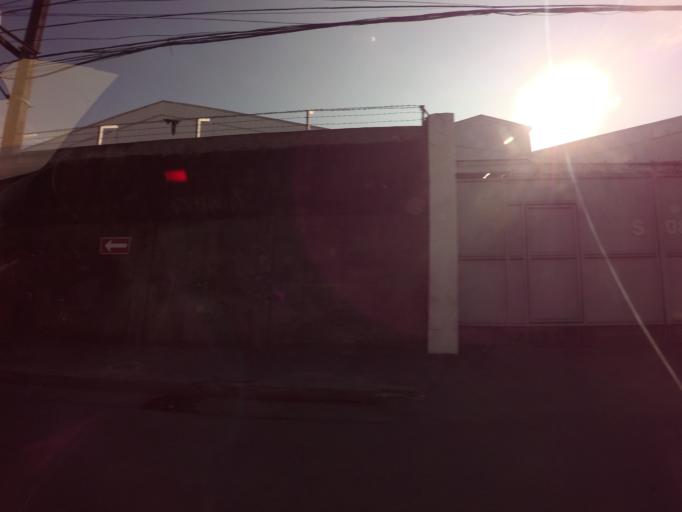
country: PH
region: Calabarzon
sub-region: Province of Rizal
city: Taguig
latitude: 14.4812
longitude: 121.0497
